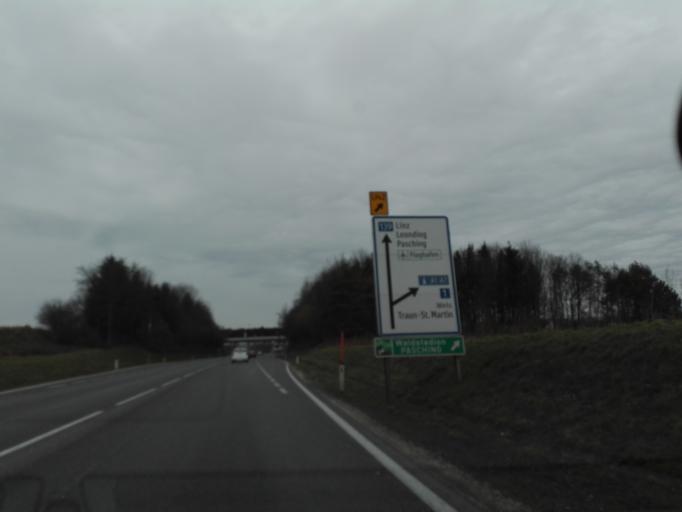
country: AT
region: Upper Austria
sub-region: Politischer Bezirk Linz-Land
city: Traun
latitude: 48.2268
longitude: 14.2234
